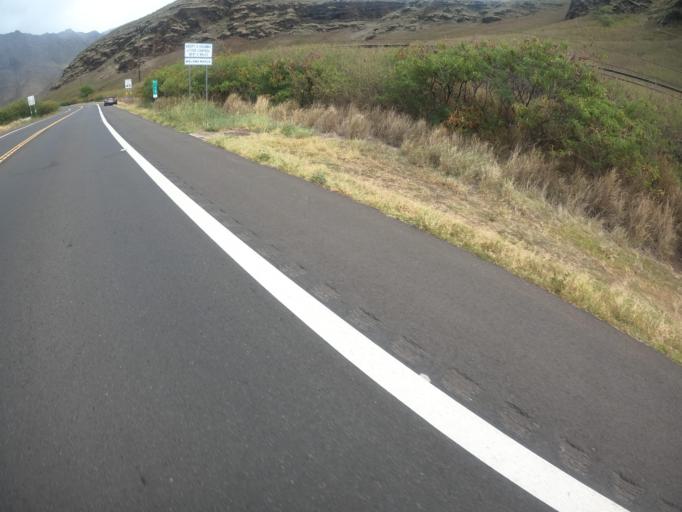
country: US
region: Hawaii
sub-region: Honolulu County
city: Makaha Valley
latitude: 21.5215
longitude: -158.2277
